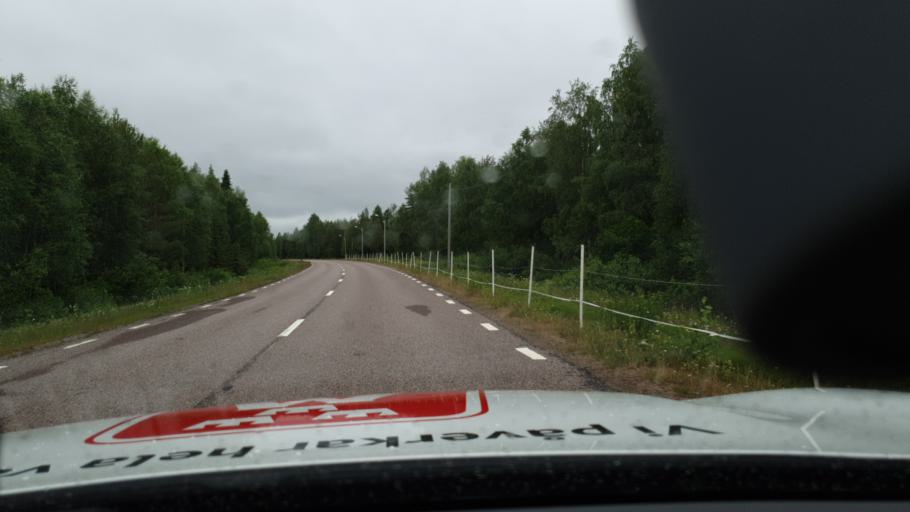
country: FI
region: Lapland
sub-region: Torniolaakso
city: Pello
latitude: 66.9565
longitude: 23.8393
